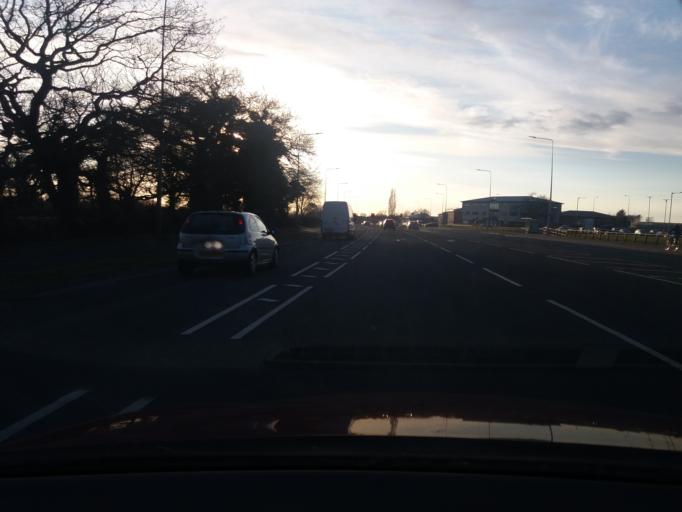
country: GB
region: England
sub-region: Lancashire
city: Euxton
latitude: 53.6716
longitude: -2.6609
